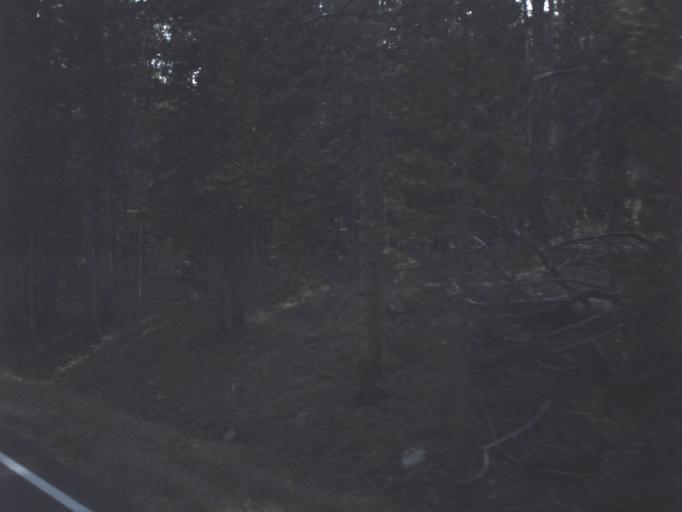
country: US
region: Utah
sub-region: Summit County
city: Oakley
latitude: 40.7986
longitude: -110.8827
